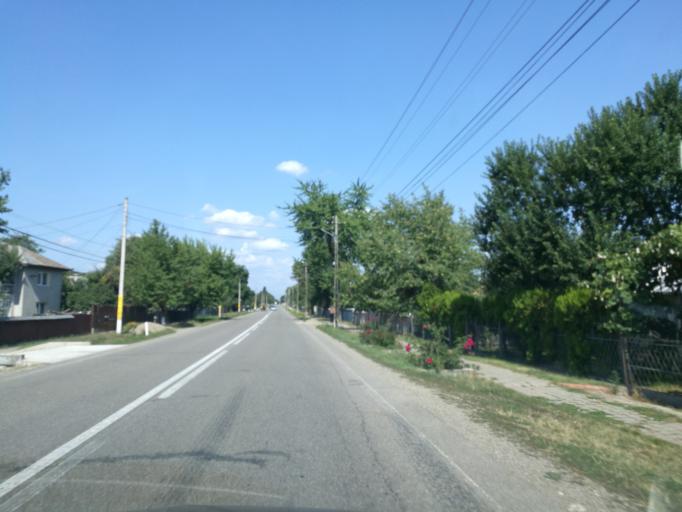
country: RO
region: Neamt
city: Bodesti
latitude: 47.0323
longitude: 26.4154
